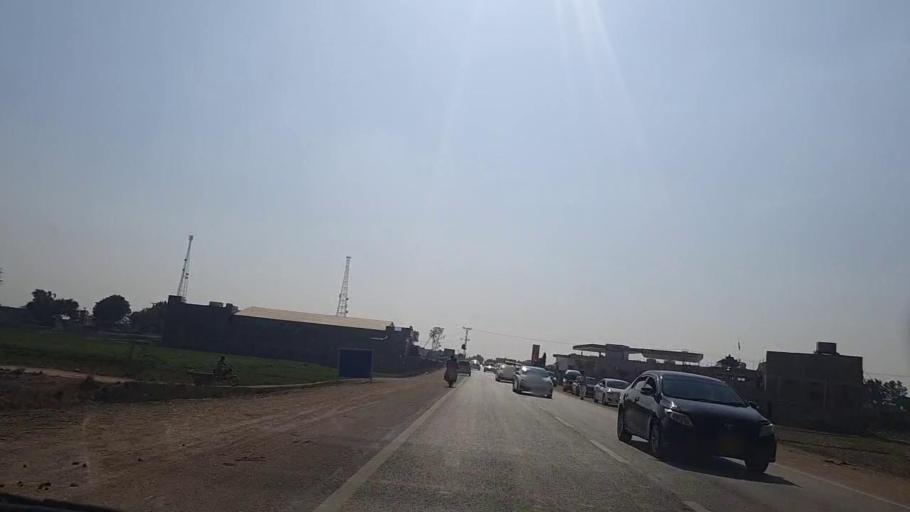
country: PK
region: Sindh
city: Hala
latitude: 25.9760
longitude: 68.3811
